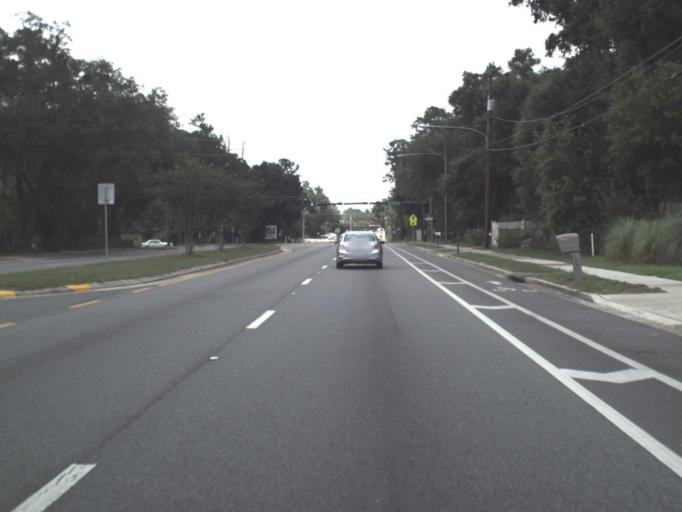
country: US
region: Florida
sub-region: Alachua County
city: Gainesville
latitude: 29.6445
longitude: -82.3114
